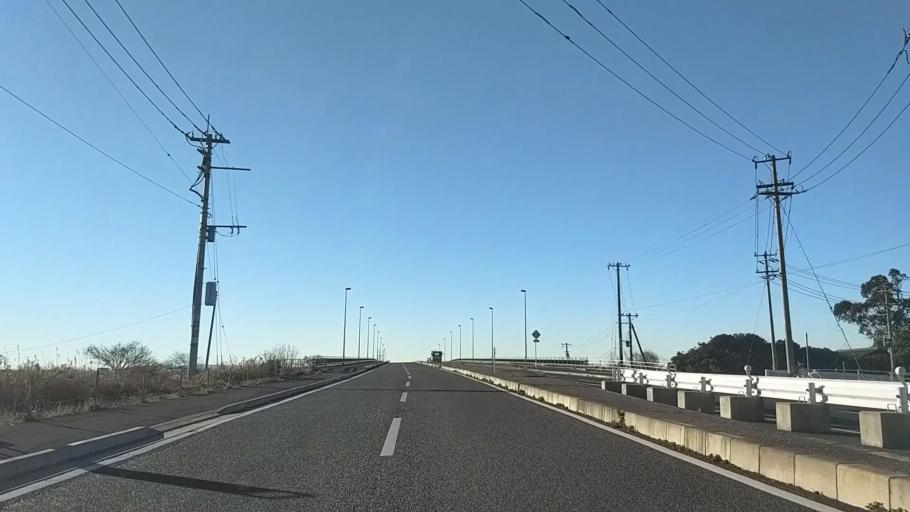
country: JP
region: Chiba
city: Kisarazu
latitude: 35.4225
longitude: 139.9197
